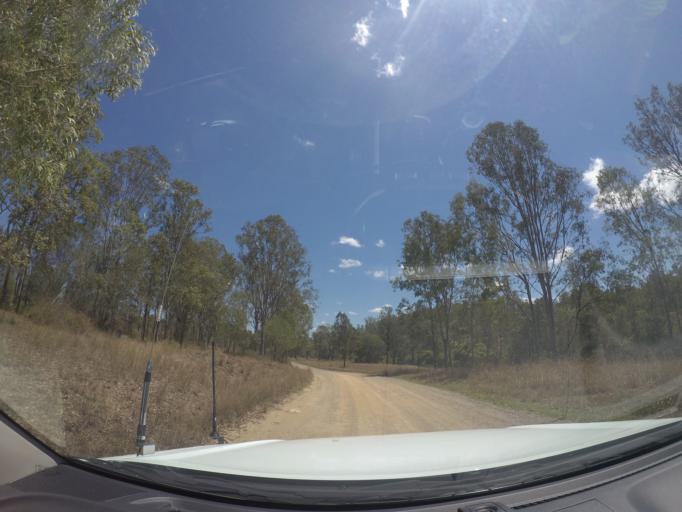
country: AU
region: Queensland
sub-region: Logan
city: North Maclean
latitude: -27.8285
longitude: 152.8643
